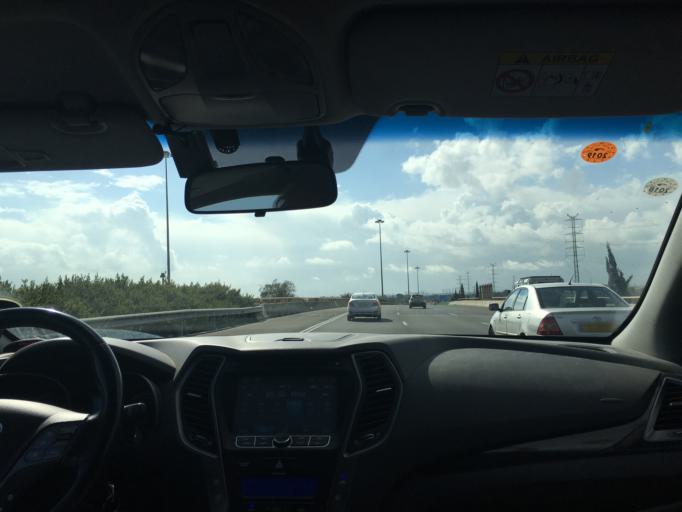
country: IL
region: Tel Aviv
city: Azor
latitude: 32.0390
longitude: 34.8297
